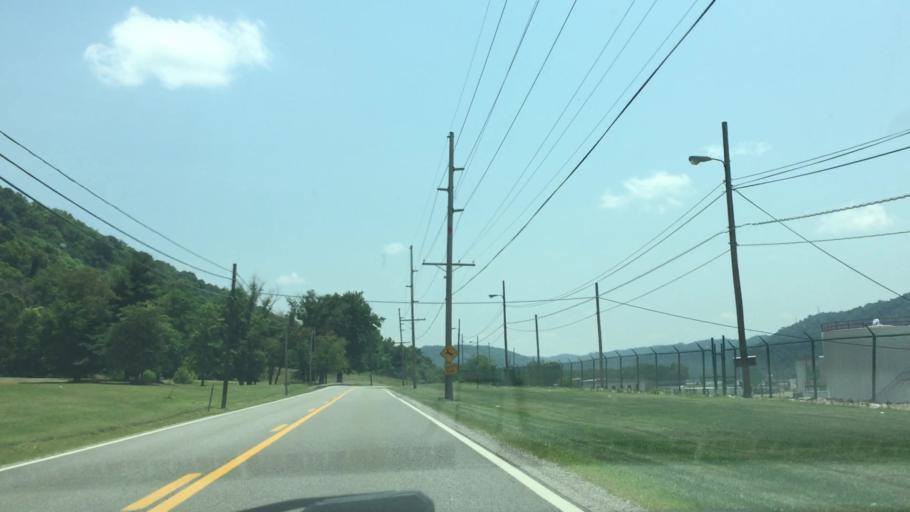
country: US
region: West Virginia
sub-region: Wetzel County
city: New Martinsville
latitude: 39.7441
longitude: -80.8452
